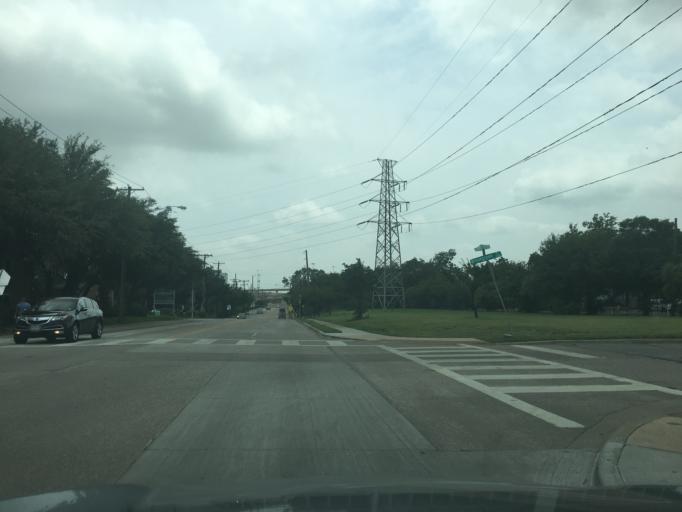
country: US
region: Texas
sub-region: Dallas County
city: Richardson
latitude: 32.9329
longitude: -96.7612
